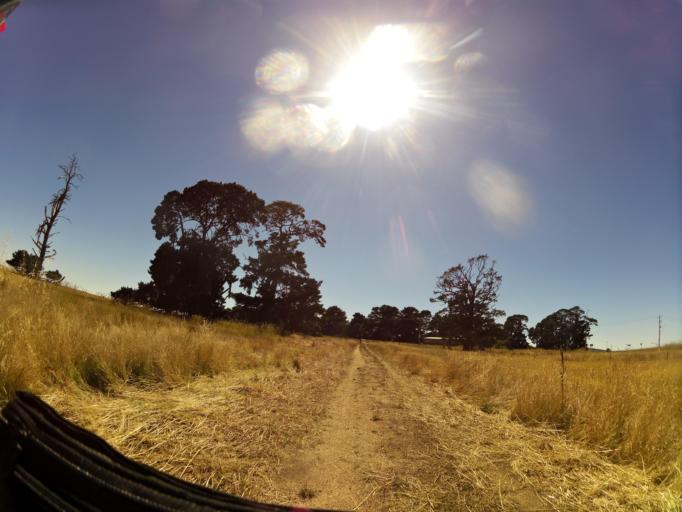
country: AU
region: Victoria
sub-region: Ballarat North
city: Delacombe
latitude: -37.6680
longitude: 143.4827
